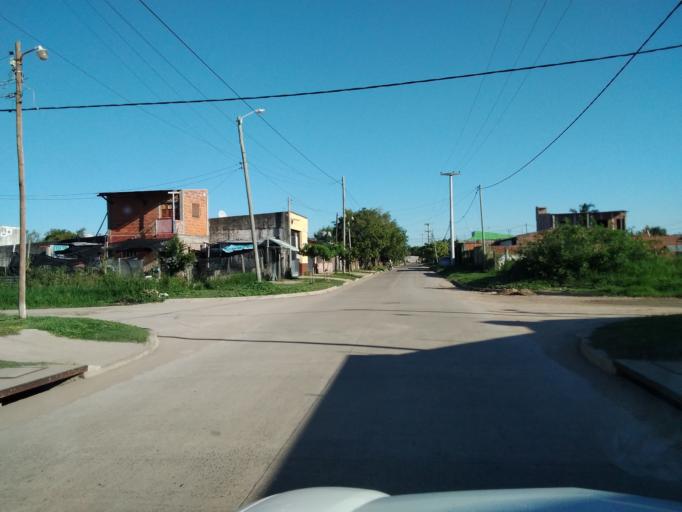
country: AR
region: Corrientes
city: Corrientes
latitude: -27.4717
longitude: -58.7915
